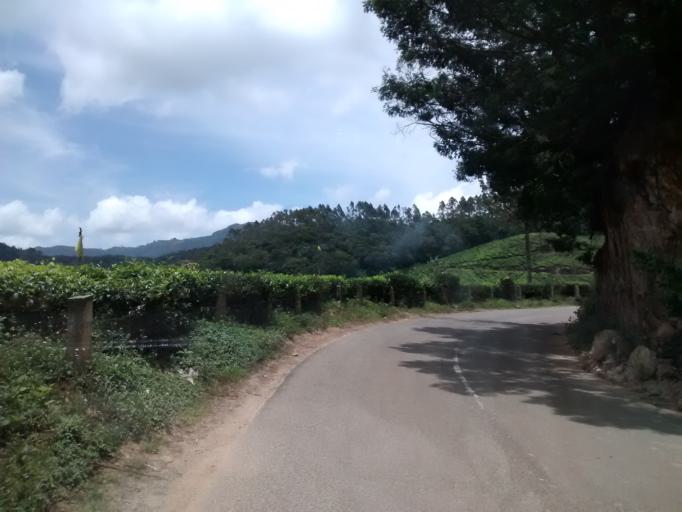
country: IN
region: Tamil Nadu
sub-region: Theni
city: Bodinayakkanur
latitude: 10.1301
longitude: 77.2337
